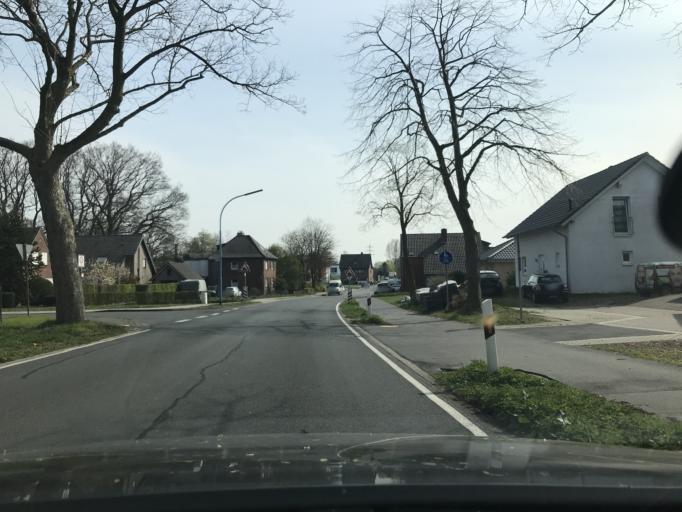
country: DE
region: North Rhine-Westphalia
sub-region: Regierungsbezirk Dusseldorf
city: Kleve
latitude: 51.7616
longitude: 6.1727
